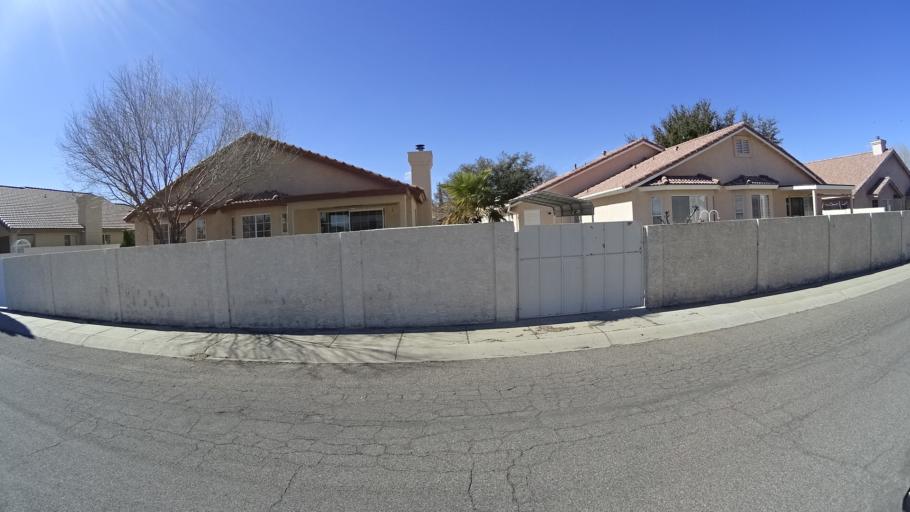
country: US
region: Arizona
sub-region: Mohave County
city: Kingman
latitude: 35.2097
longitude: -114.0401
